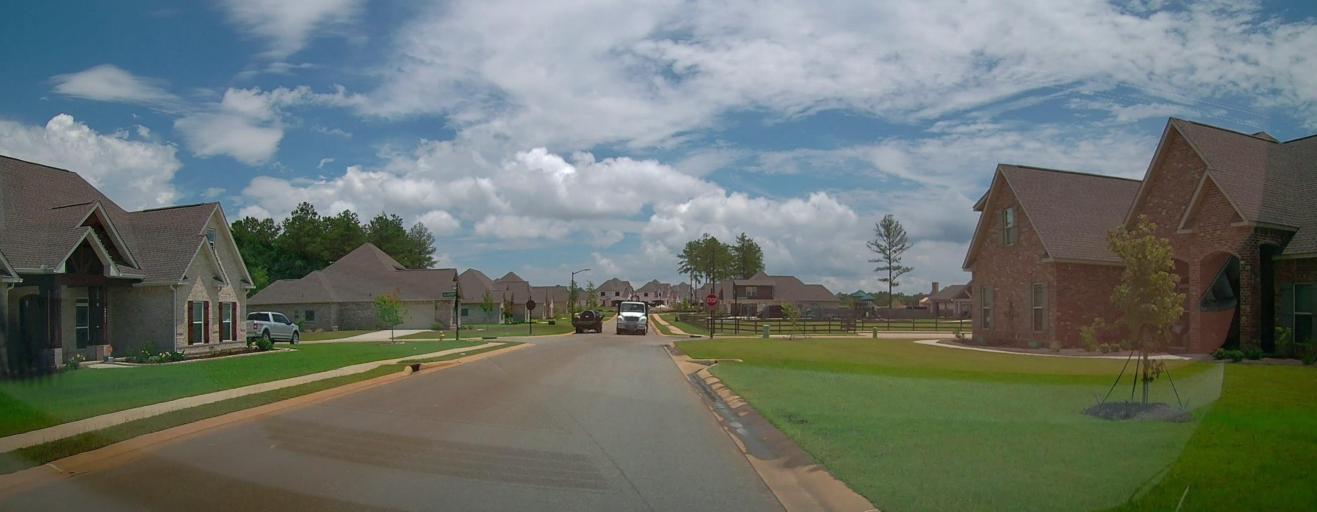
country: US
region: Georgia
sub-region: Houston County
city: Robins Air Force Base
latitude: 32.5151
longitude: -83.6318
